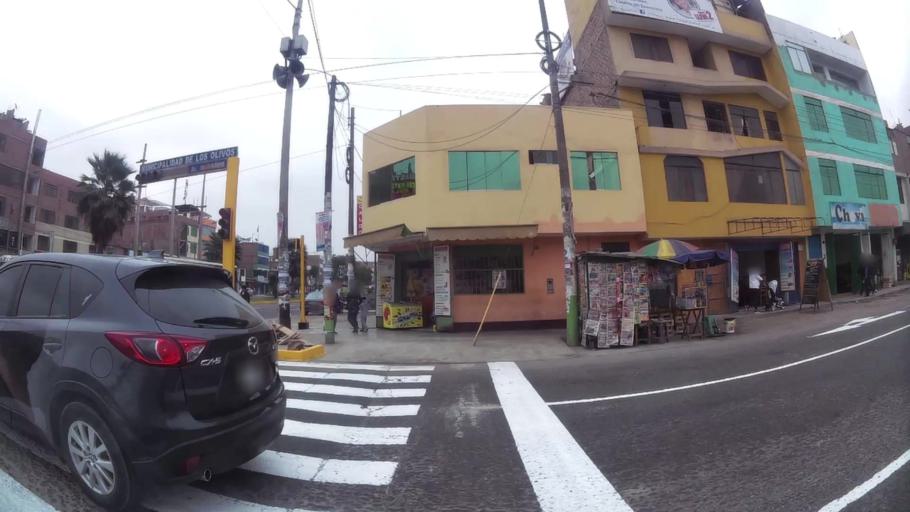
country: PE
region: Lima
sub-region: Lima
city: Independencia
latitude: -11.9700
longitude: -77.0800
